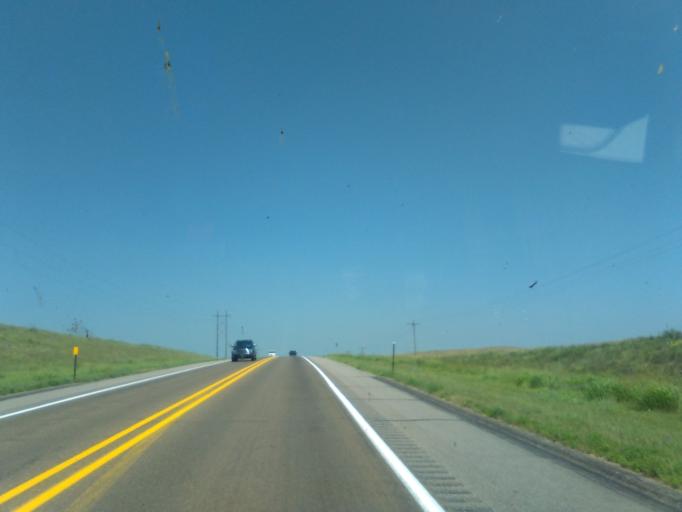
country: US
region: Nebraska
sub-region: Lincoln County
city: North Platte
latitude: 40.8311
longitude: -100.7538
